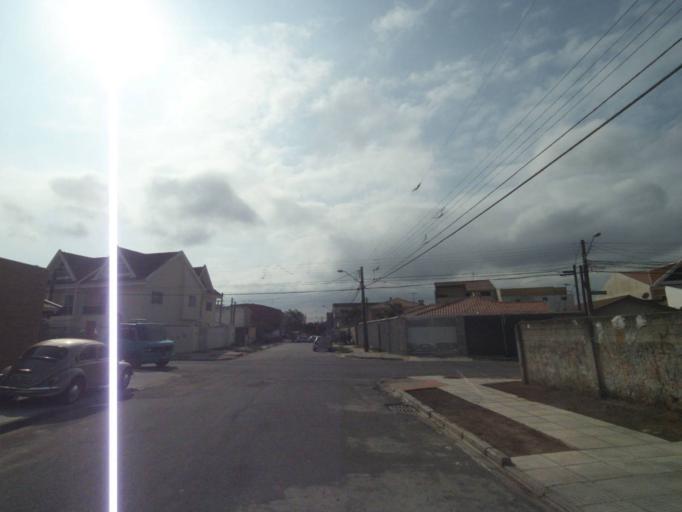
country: BR
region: Parana
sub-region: Sao Jose Dos Pinhais
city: Sao Jose dos Pinhais
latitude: -25.5403
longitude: -49.2588
